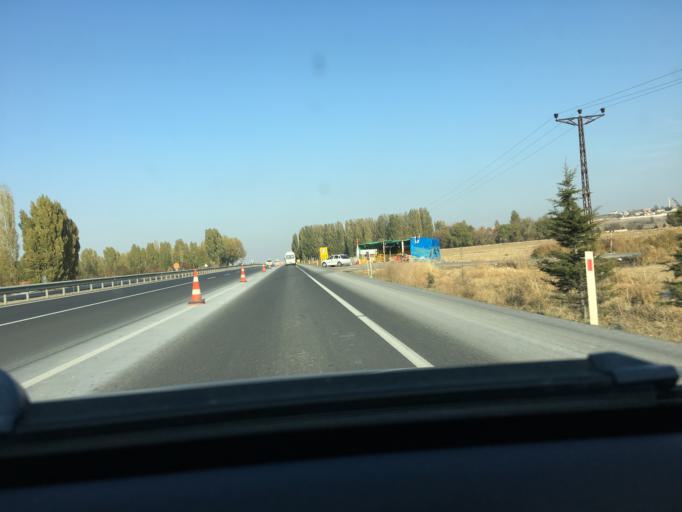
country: TR
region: Ankara
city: Temelli
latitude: 39.6892
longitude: 32.2522
